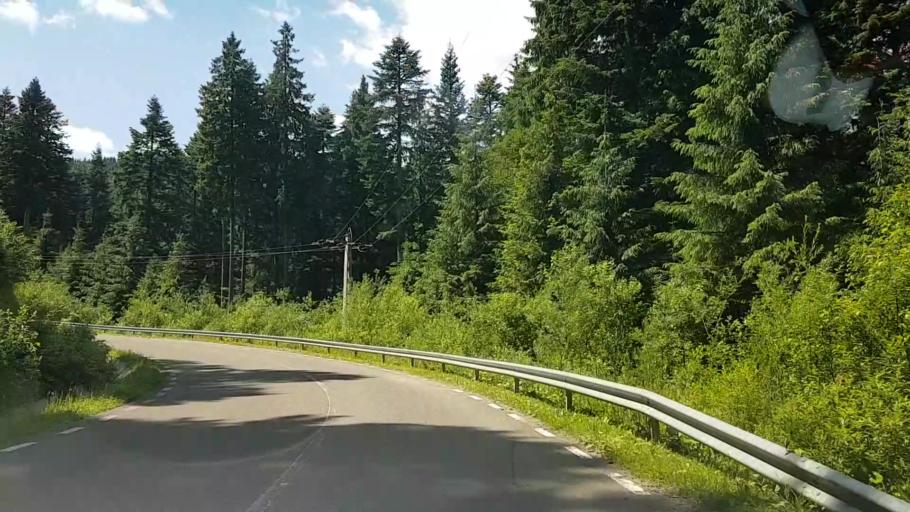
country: RO
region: Suceava
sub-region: Comuna Sadova
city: Sadova
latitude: 47.4718
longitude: 25.5126
